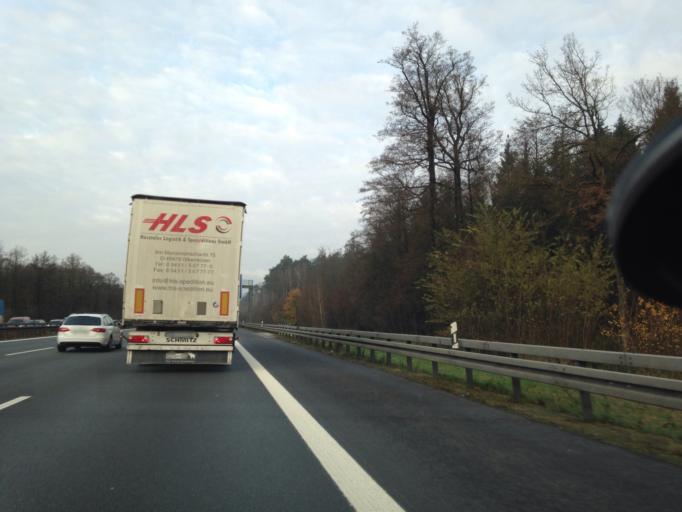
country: DE
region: Bavaria
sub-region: Regierungsbezirk Mittelfranken
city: Buckenhof
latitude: 49.5337
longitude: 11.0466
